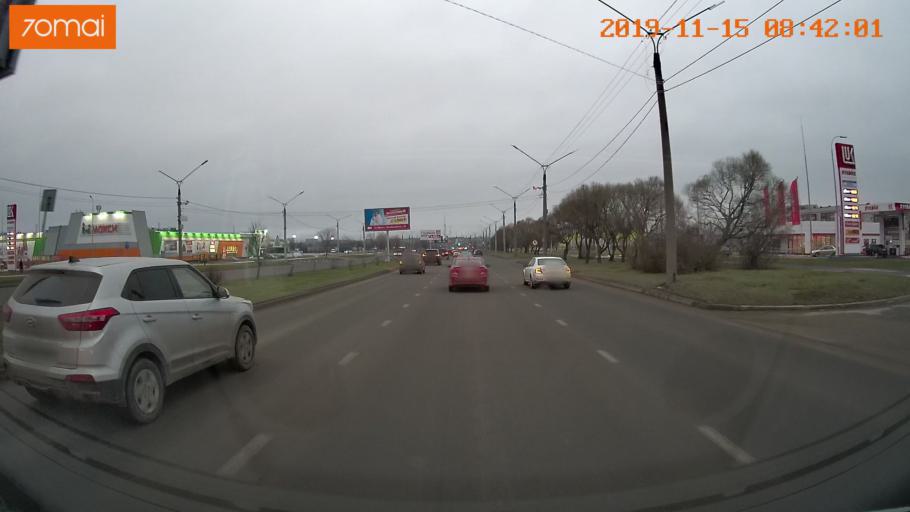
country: RU
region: Vologda
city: Cherepovets
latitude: 59.0998
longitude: 37.9101
